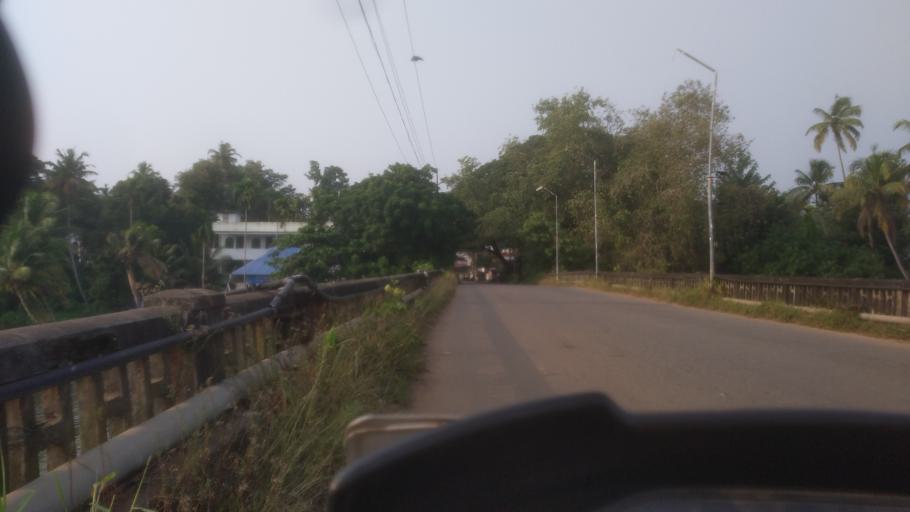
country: IN
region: Kerala
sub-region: Alappuzha
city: Arukutti
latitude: 9.8442
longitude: 76.3871
